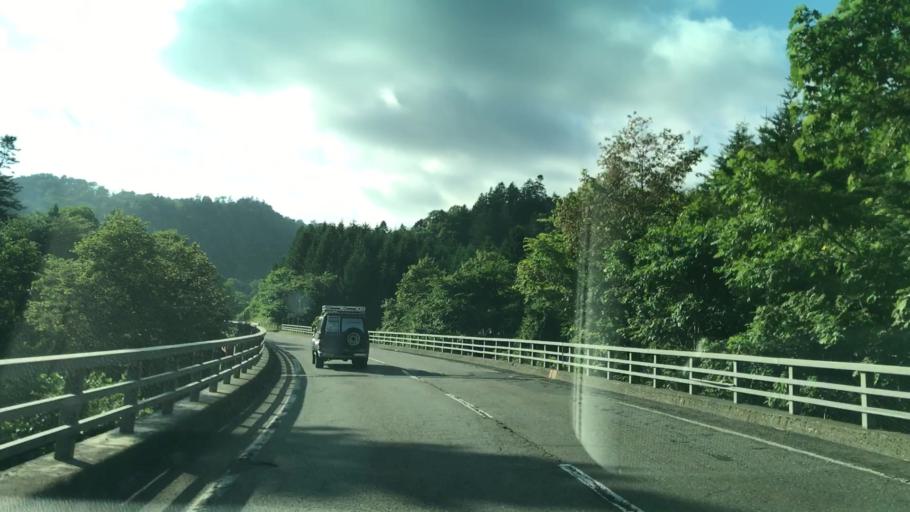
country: JP
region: Hokkaido
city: Iwamizawa
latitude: 42.9086
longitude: 142.1256
